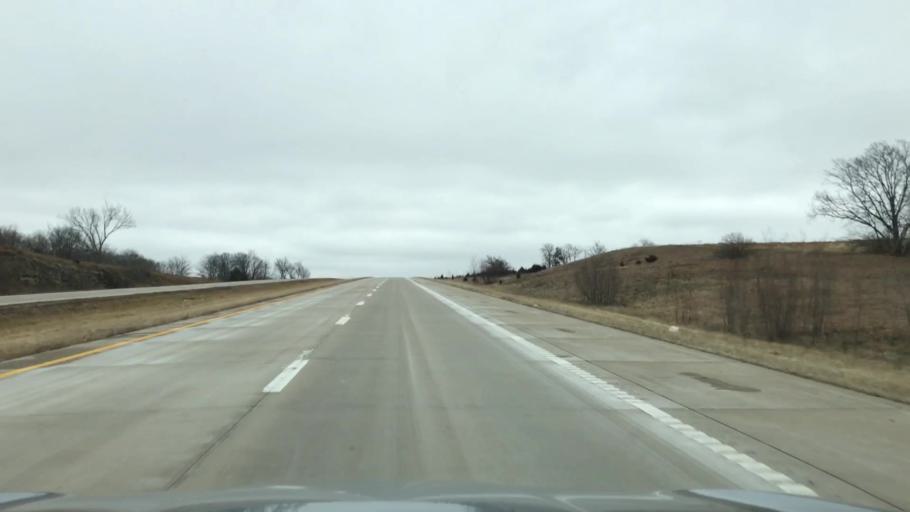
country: US
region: Missouri
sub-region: Livingston County
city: Chillicothe
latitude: 39.7356
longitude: -93.7500
